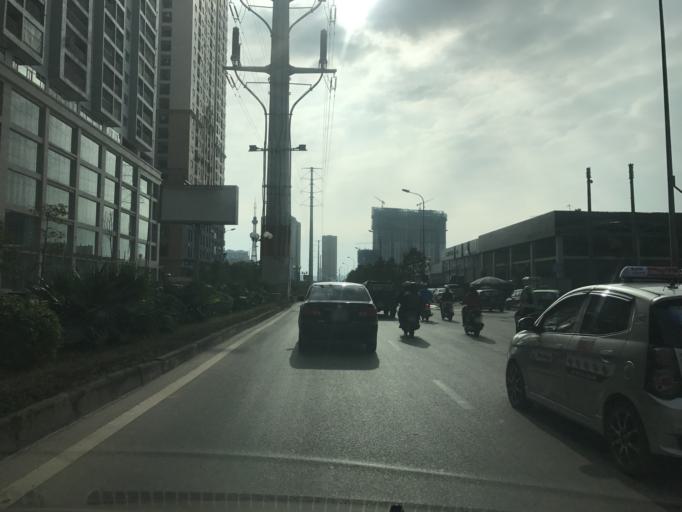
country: VN
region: Ha Noi
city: Thanh Xuan
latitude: 20.9975
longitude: 105.7942
